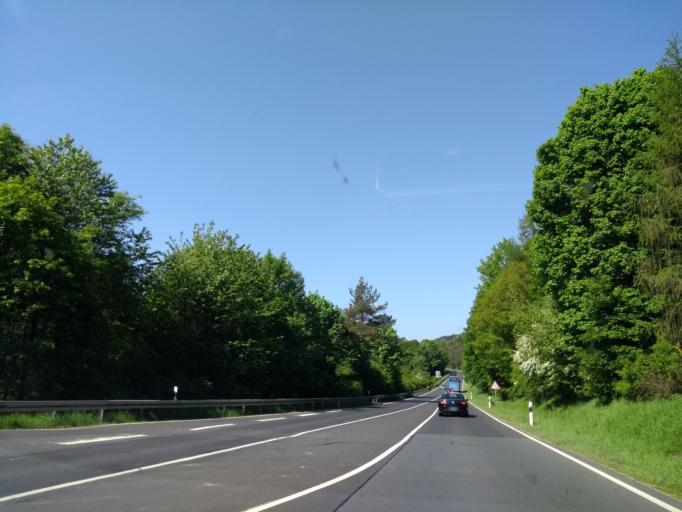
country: DE
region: Hesse
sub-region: Regierungsbezirk Darmstadt
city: Friedrichsdorf
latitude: 50.2812
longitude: 8.6305
